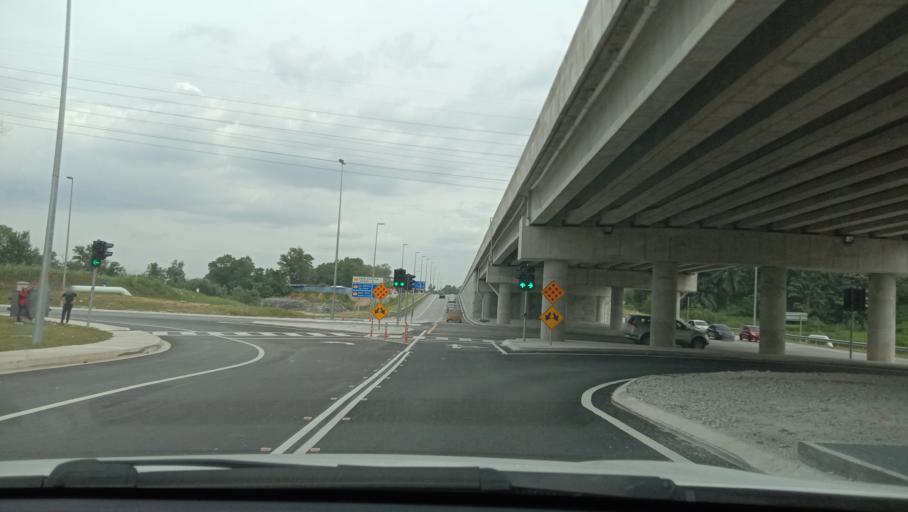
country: MY
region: Selangor
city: Kampung Baru Subang
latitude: 3.1267
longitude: 101.5194
